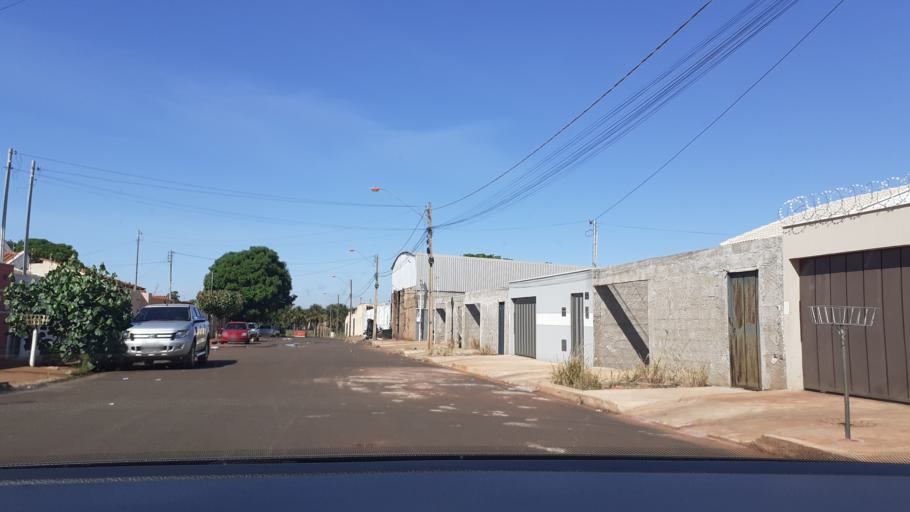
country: BR
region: Goias
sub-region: Itumbiara
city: Itumbiara
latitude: -18.4069
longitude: -49.2539
